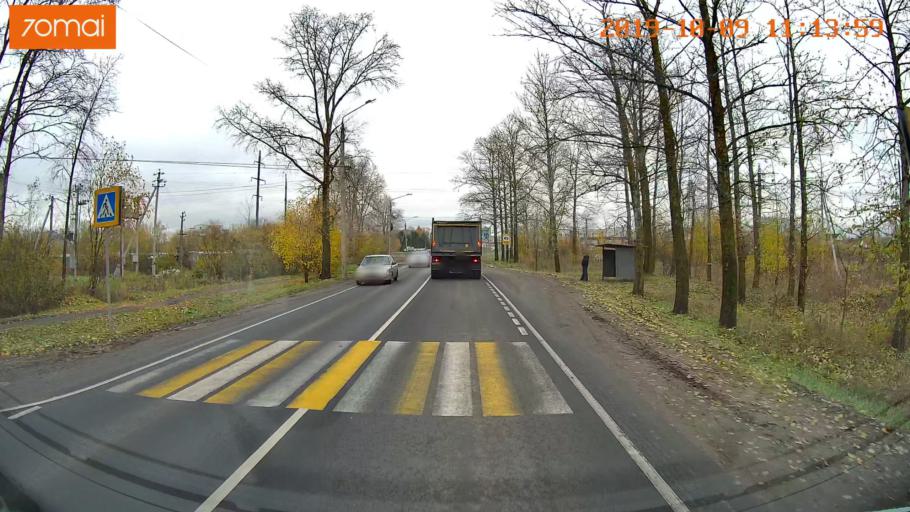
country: RU
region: Vologda
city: Vologda
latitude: 59.1855
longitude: 39.8490
